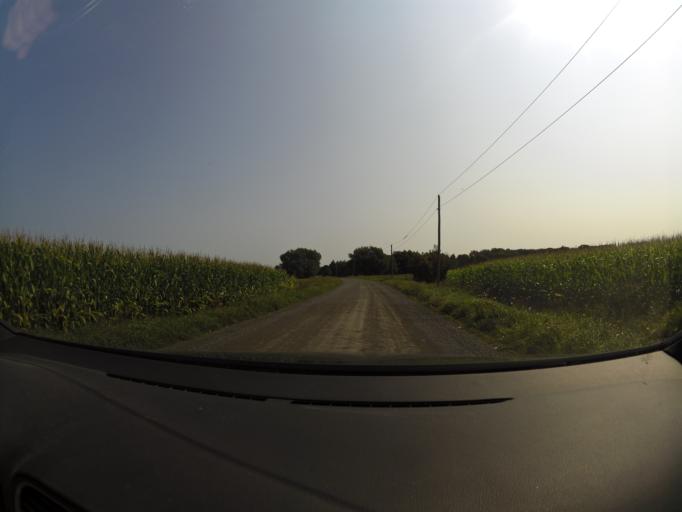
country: CA
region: Ontario
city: Carleton Place
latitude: 45.3524
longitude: -76.0836
